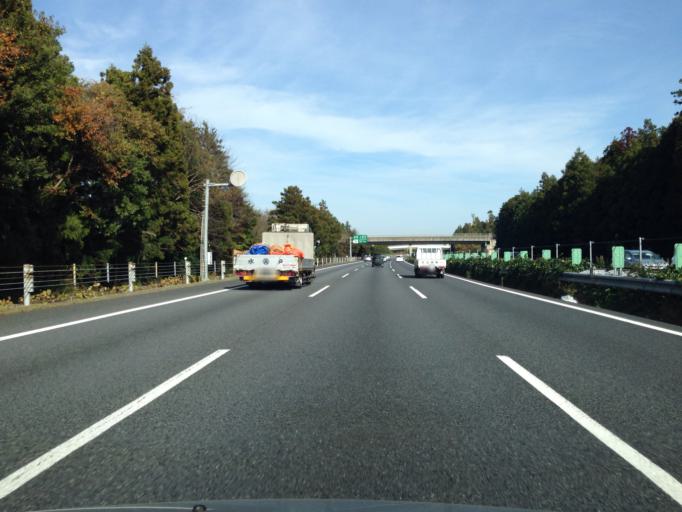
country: JP
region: Ibaraki
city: Tomobe
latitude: 36.2736
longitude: 140.3075
